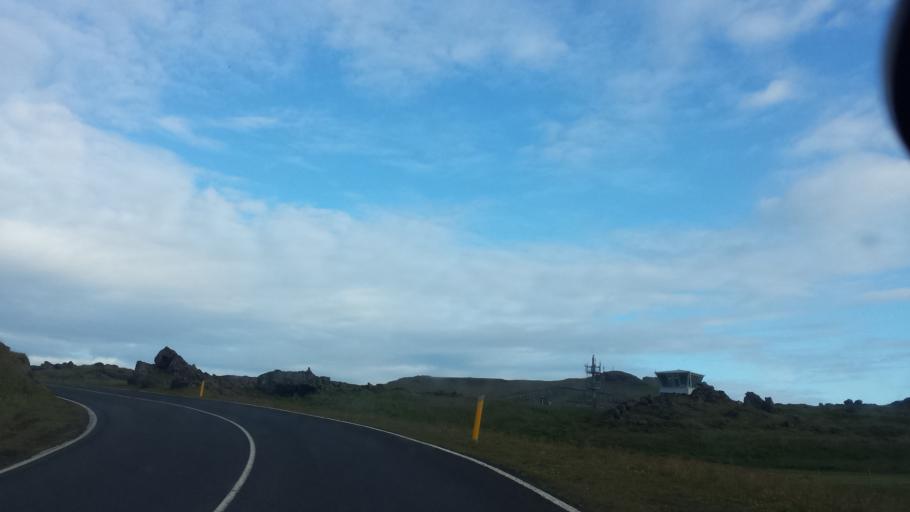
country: IS
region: South
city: Vestmannaeyjar
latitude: 63.4273
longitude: -20.2743
